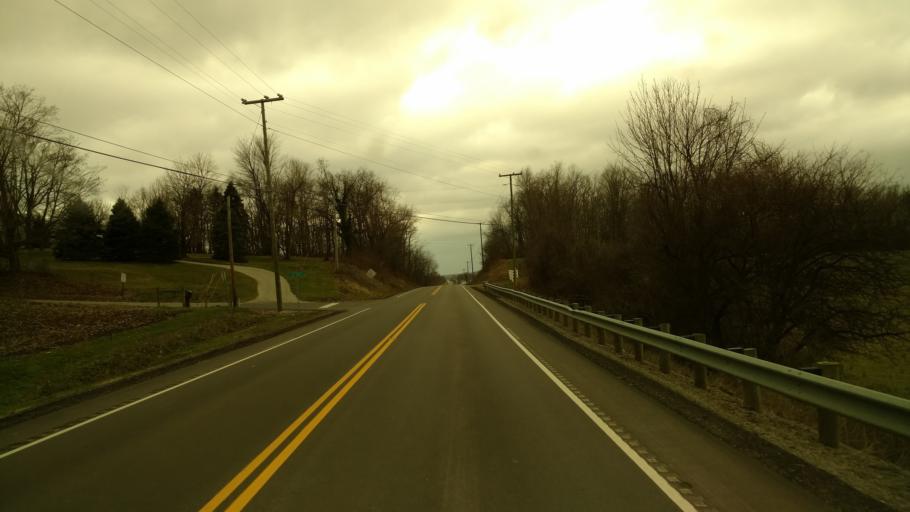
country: US
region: Ohio
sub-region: Licking County
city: Harbor Hills
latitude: 39.9597
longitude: -82.4214
